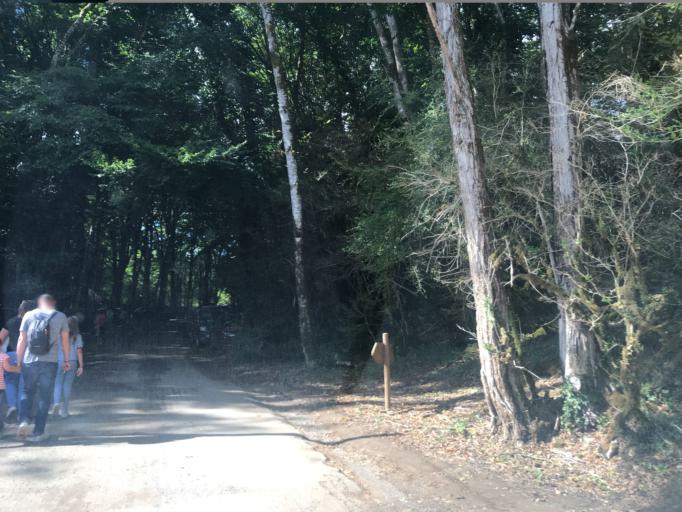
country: FR
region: Aquitaine
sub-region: Departement de la Dordogne
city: Saint-Cyprien
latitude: 44.9696
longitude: 1.0329
